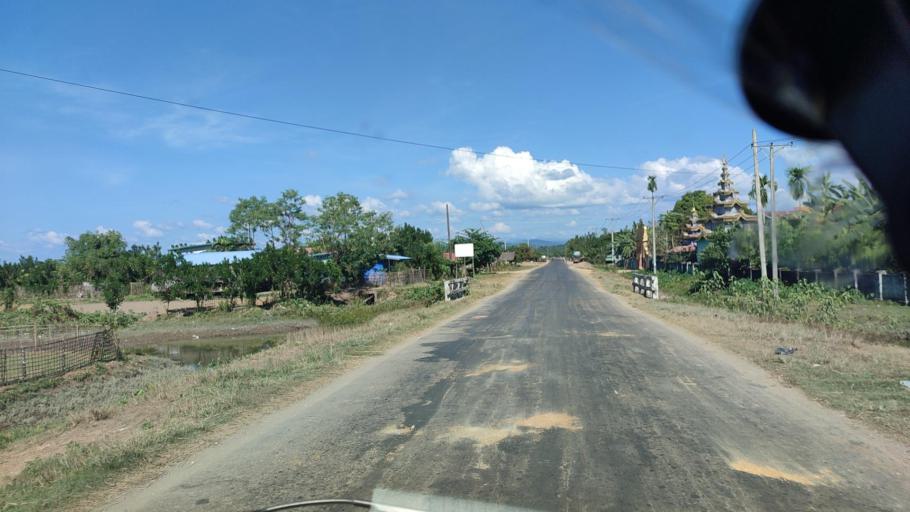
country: MM
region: Rakhine
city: Sittwe
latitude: 20.4080
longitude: 93.3027
